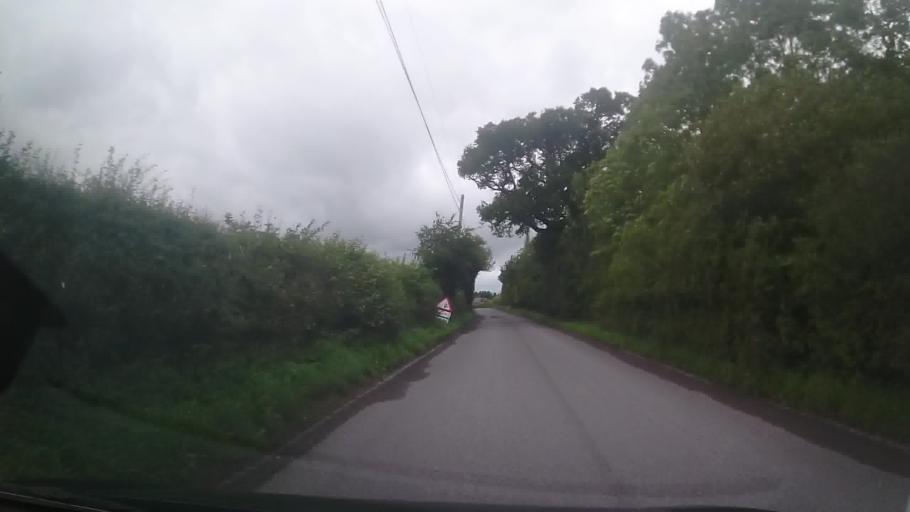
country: GB
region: England
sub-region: Shropshire
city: Petton
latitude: 52.8505
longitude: -2.8365
